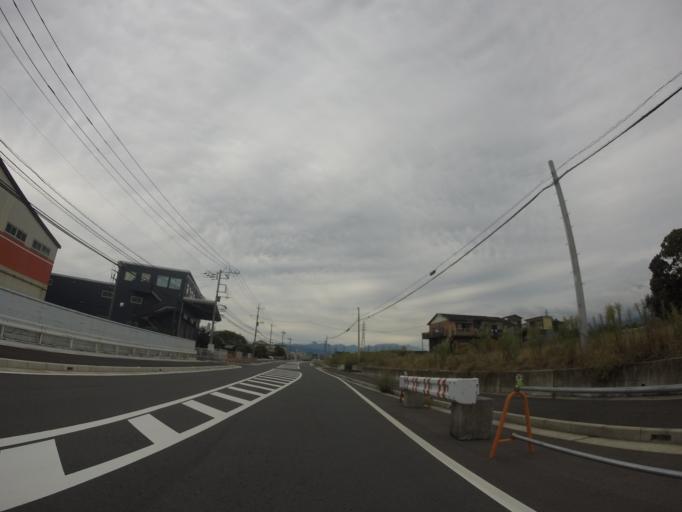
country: JP
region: Shizuoka
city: Fuji
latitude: 35.1989
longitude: 138.6752
